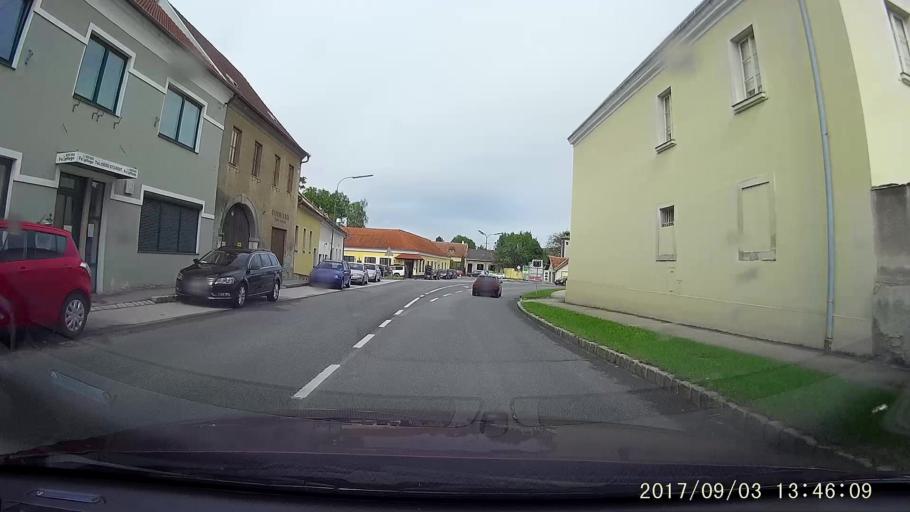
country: AT
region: Lower Austria
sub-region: Politischer Bezirk Hollabrunn
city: Guntersdorf
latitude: 48.6488
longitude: 16.0470
